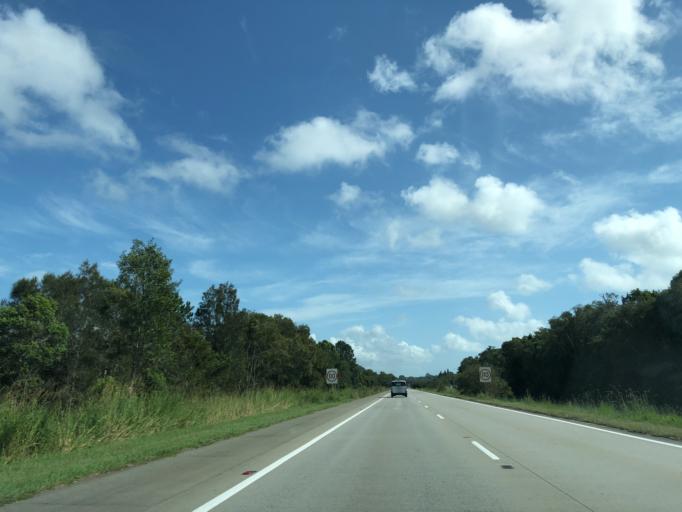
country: AU
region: New South Wales
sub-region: Byron Shire
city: Brunswick Heads
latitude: -28.5915
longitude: 153.5445
